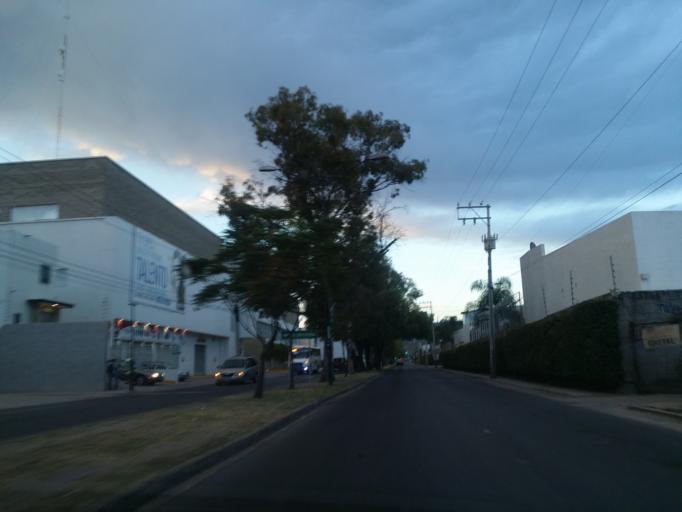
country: MX
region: Guanajuato
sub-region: Leon
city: Medina
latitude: 21.1512
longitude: -101.6481
